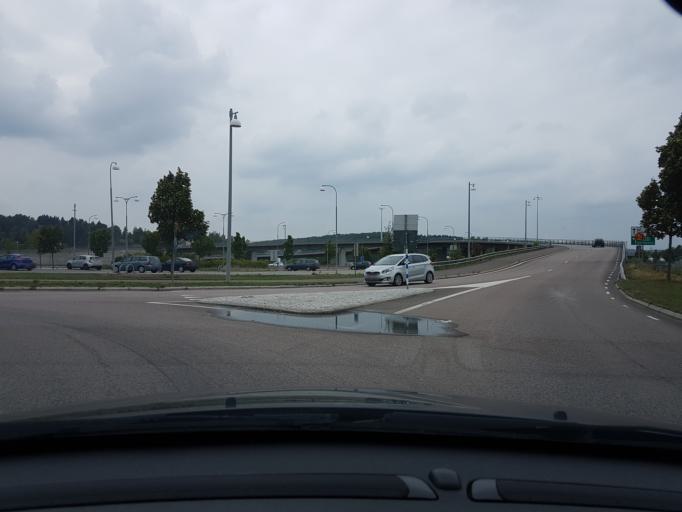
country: SE
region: Vaestra Goetaland
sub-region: Ale Kommun
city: Nodinge-Nol
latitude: 57.9195
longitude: 12.0658
